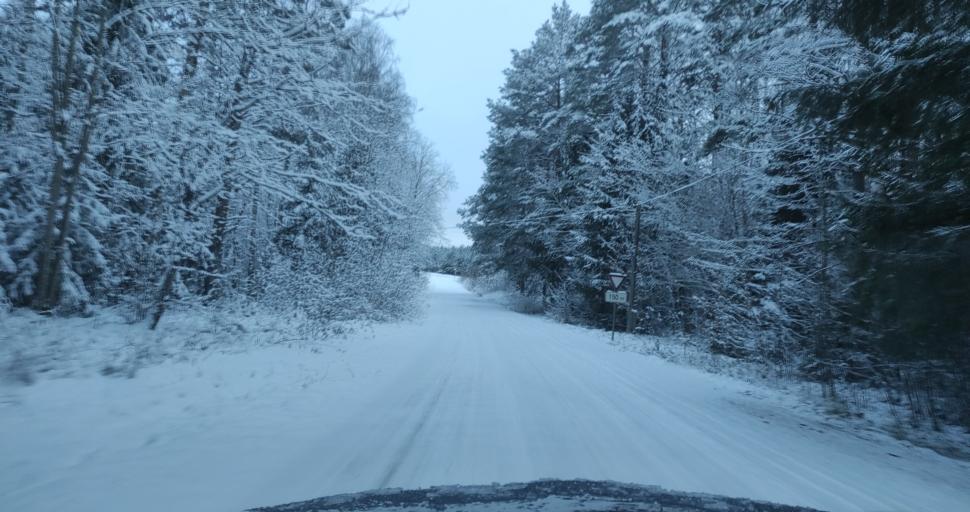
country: LV
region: Alsunga
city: Alsunga
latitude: 56.9614
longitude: 21.6023
